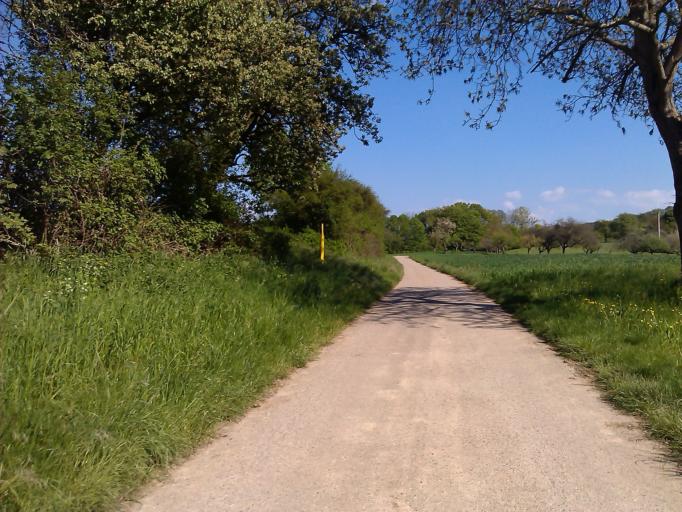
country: DE
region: Baden-Wuerttemberg
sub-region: Karlsruhe Region
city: Kurnbach
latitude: 49.0681
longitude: 8.8396
